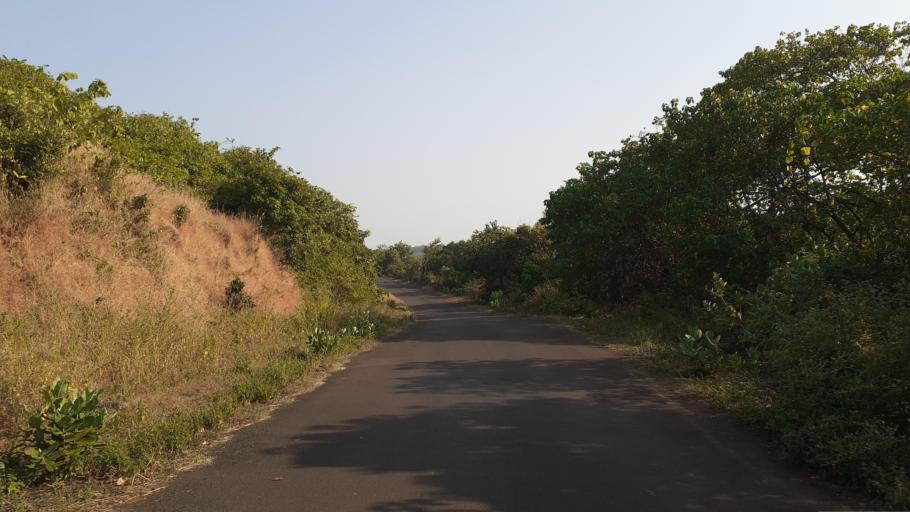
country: IN
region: Maharashtra
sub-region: Ratnagiri
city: Ratnagiri
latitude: 17.2199
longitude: 73.2462
